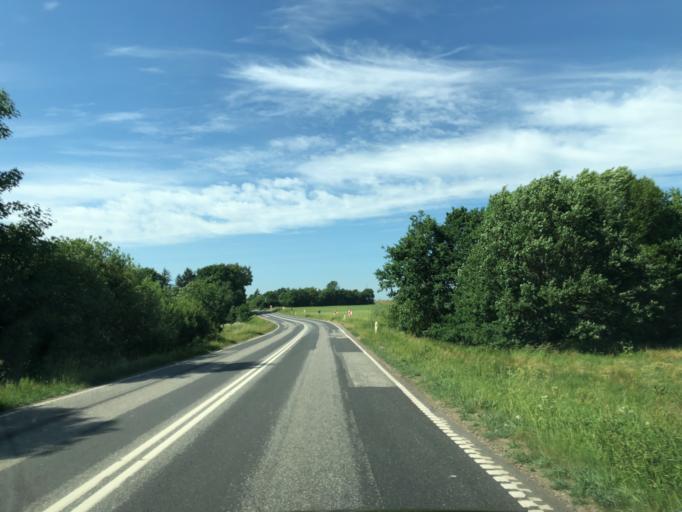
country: DK
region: South Denmark
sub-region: Vejle Kommune
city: Give
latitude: 55.8844
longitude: 9.2205
